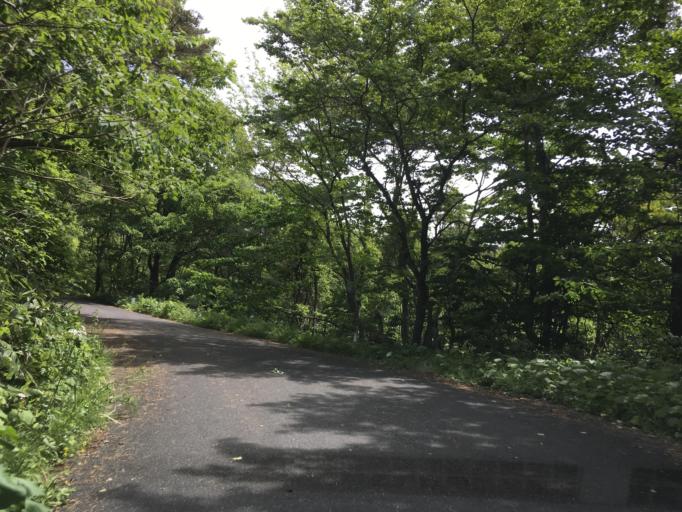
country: JP
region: Iwate
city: Mizusawa
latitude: 39.1245
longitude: 141.2990
